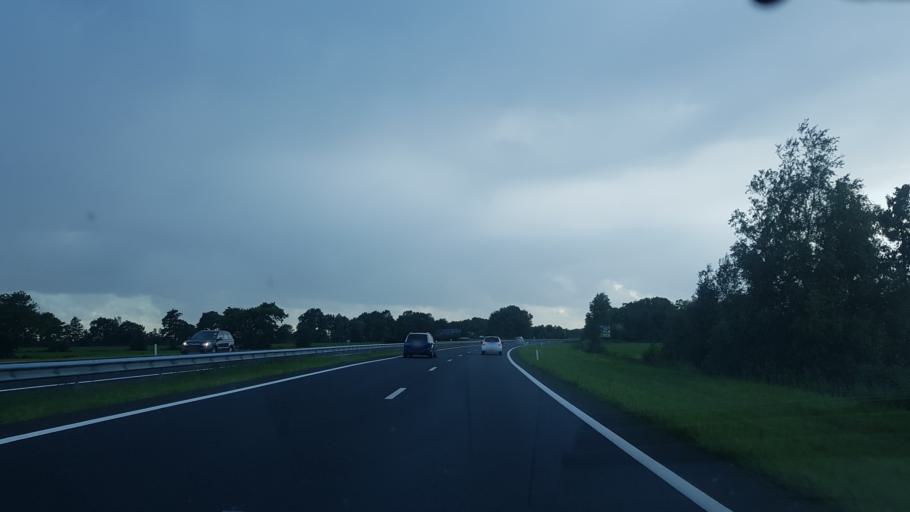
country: NL
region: Friesland
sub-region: Gemeente Smallingerland
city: Oudega
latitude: 53.1449
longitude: 5.9977
